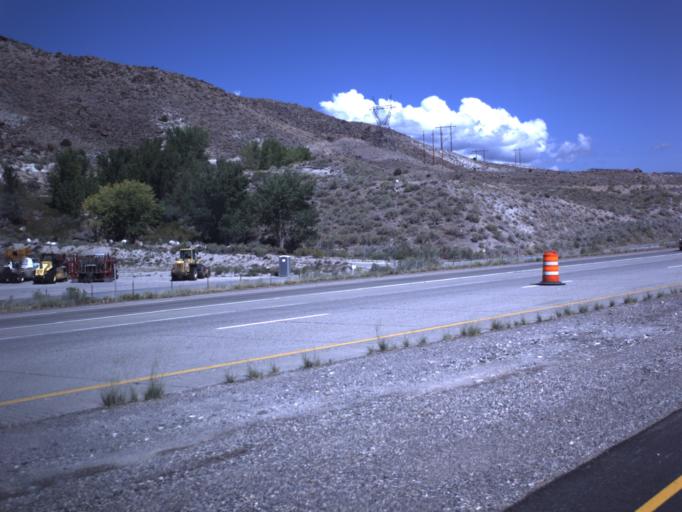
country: US
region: Utah
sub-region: Sevier County
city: Richfield
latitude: 38.7443
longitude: -112.1092
